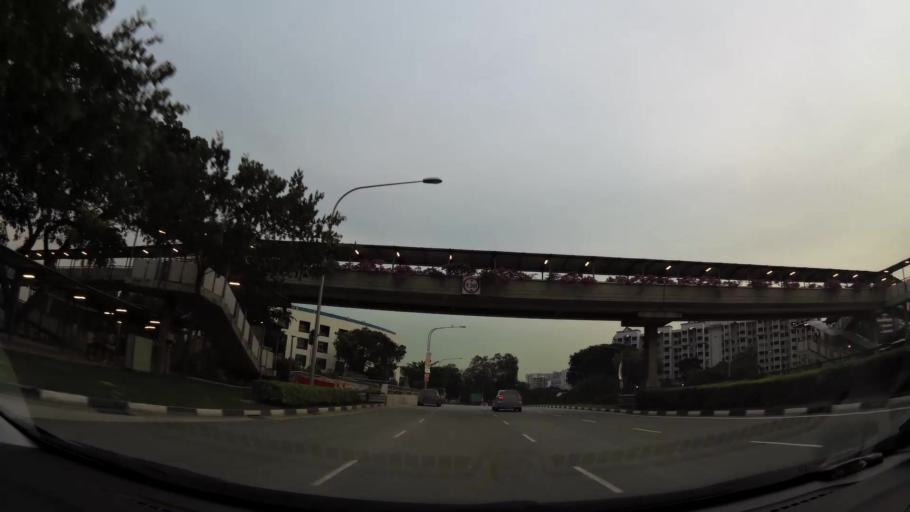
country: SG
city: Singapore
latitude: 1.3050
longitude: 103.8835
